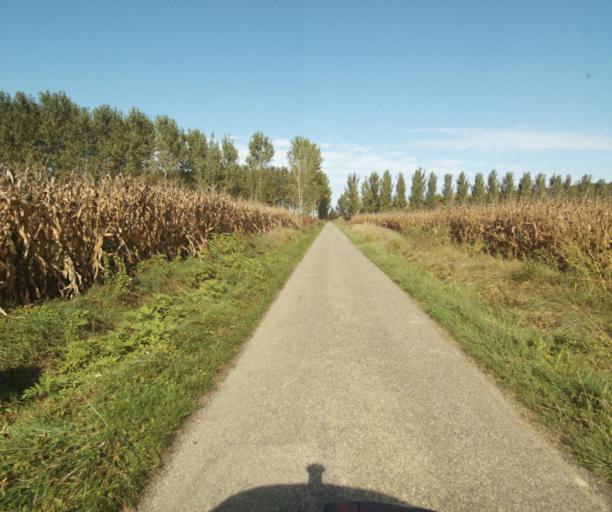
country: FR
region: Midi-Pyrenees
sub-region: Departement du Tarn-et-Garonne
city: Finhan
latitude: 43.9059
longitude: 1.2163
